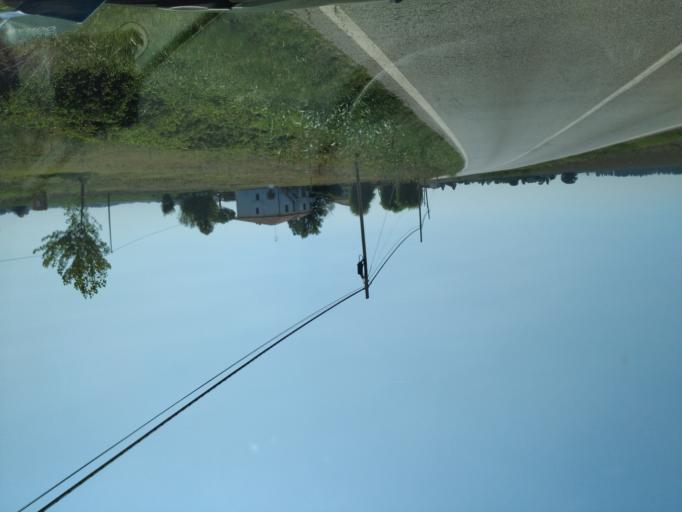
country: IT
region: Emilia-Romagna
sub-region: Provincia di Ferrara
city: Coccanile-Cesta
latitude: 44.8861
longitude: 11.8584
